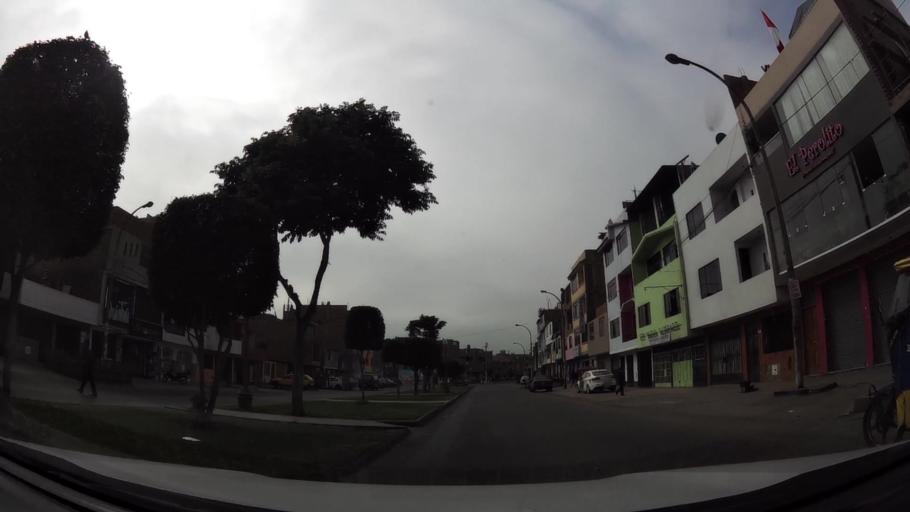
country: PE
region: Callao
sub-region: Callao
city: Callao
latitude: -12.0265
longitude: -77.0944
